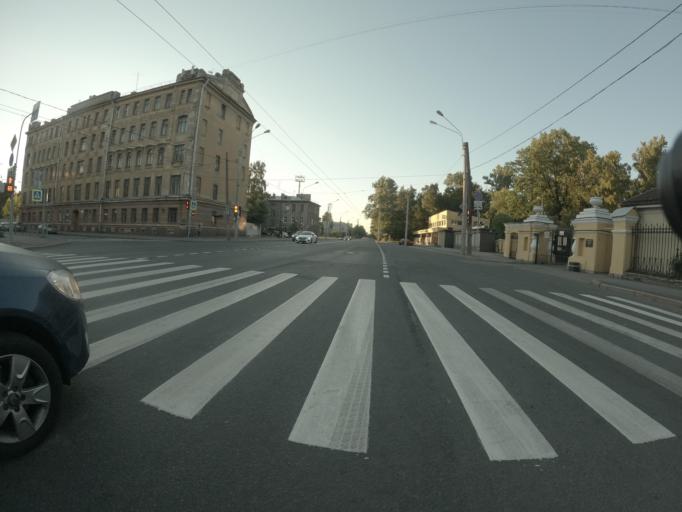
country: RU
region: Leningrad
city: Kalininskiy
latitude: 59.9463
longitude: 30.4208
